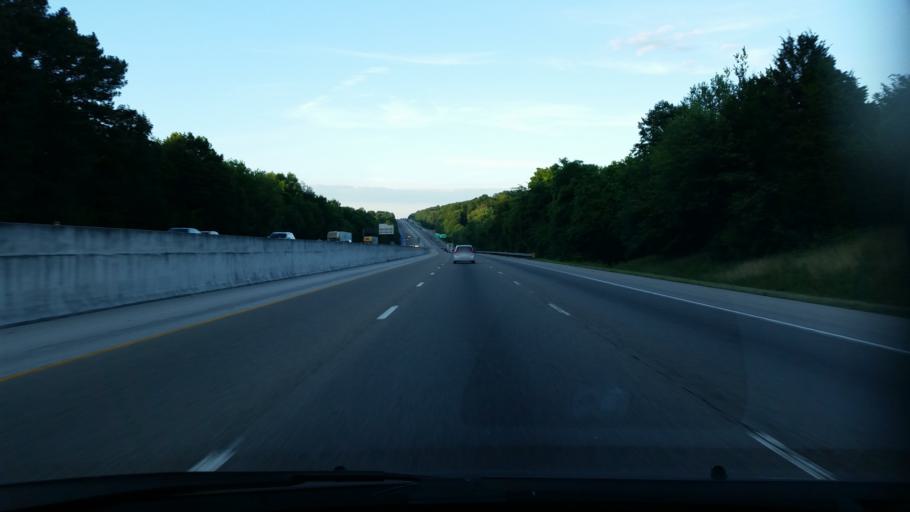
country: US
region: Tennessee
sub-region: Jefferson County
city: Dandridge
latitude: 36.0458
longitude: -83.4234
